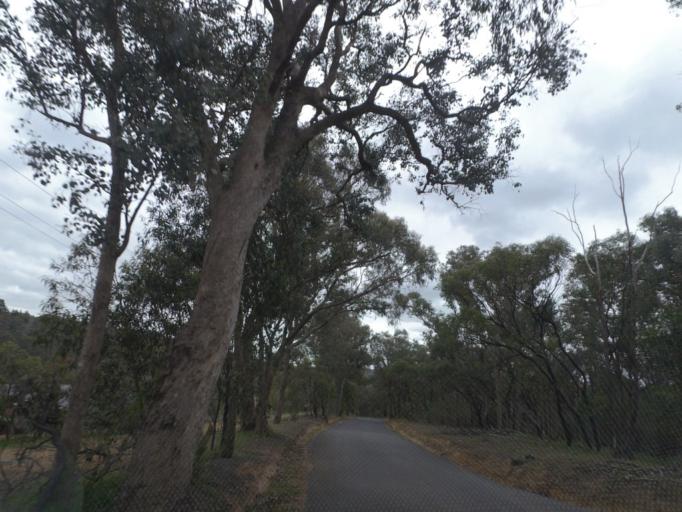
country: AU
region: Victoria
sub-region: Nillumbik
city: Hurstbridge
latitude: -37.6421
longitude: 145.2057
